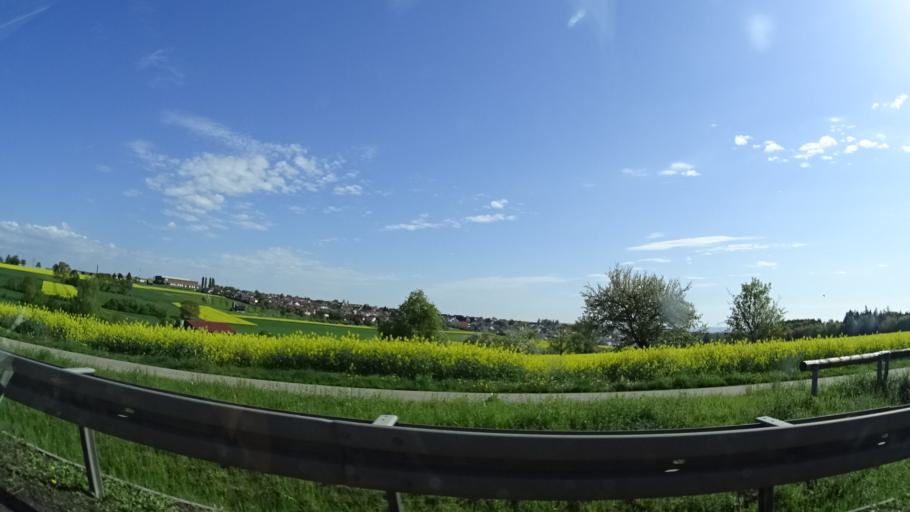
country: DE
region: Baden-Wuerttemberg
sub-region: Regierungsbezirk Stuttgart
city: Motzingen
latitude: 48.5252
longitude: 8.7639
